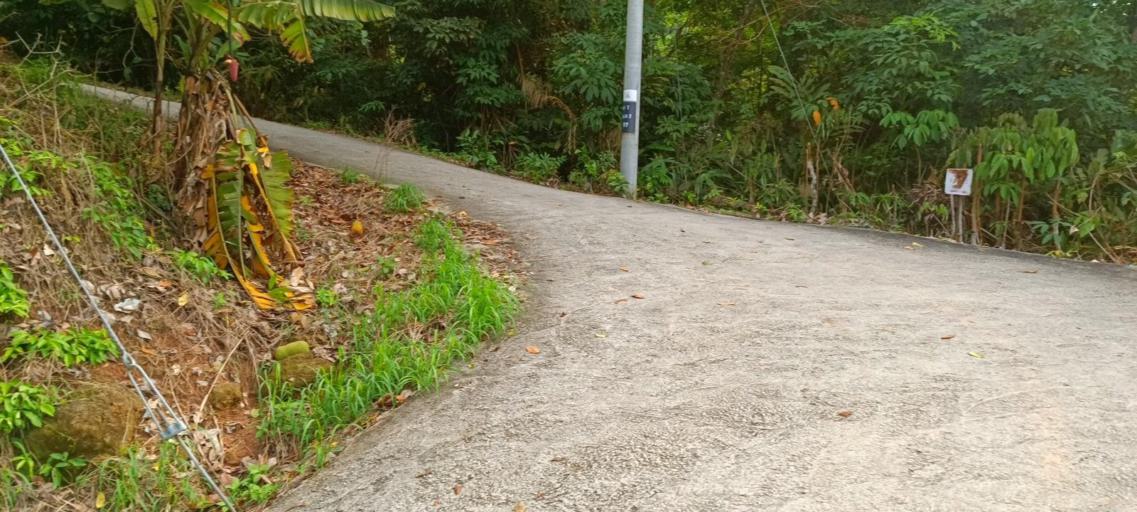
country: MY
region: Penang
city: Kampung Sungai Ara
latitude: 5.3787
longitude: 100.2454
